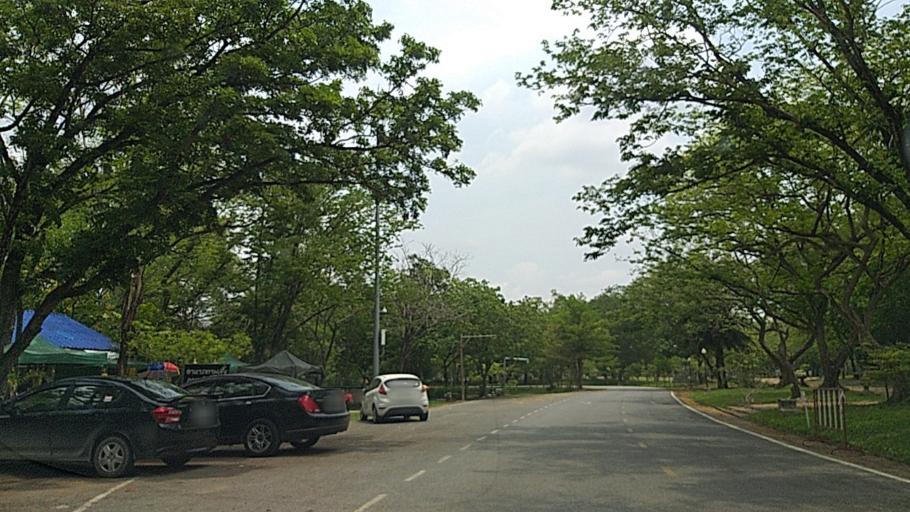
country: TH
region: Bangkok
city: Thawi Watthana
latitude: 13.7806
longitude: 100.3201
